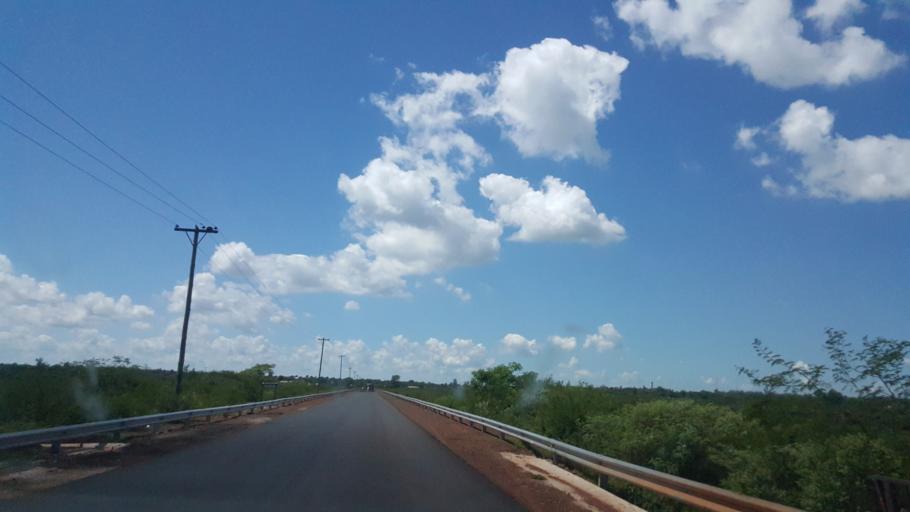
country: AR
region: Corrientes
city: Santo Tome
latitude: -28.5315
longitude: -56.0531
